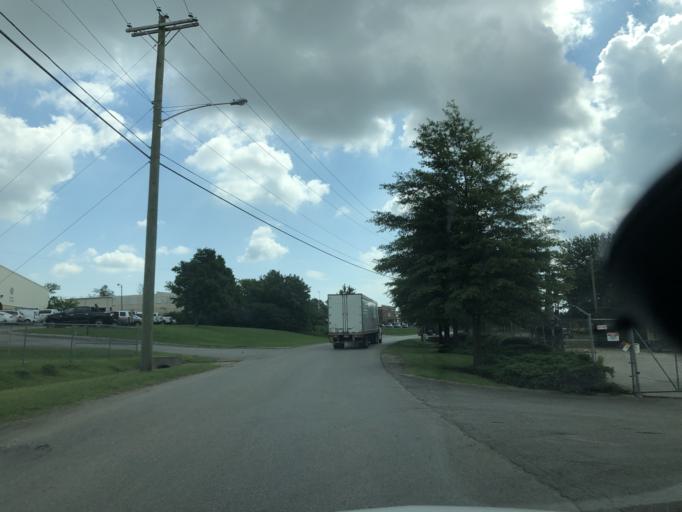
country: US
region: Tennessee
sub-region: Rutherford County
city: La Vergne
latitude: 36.0118
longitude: -86.6085
